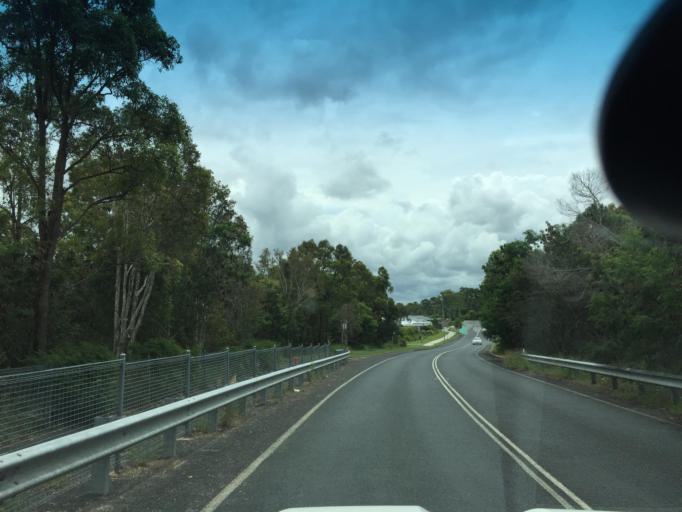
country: AU
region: Queensland
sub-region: Moreton Bay
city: Caboolture
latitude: -27.0670
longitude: 152.9329
